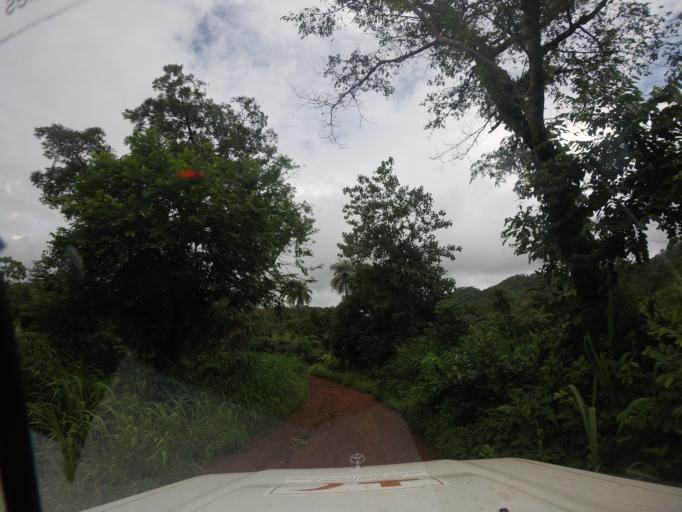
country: SL
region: Northern Province
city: Kamakwie
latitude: 9.6790
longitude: -12.2366
